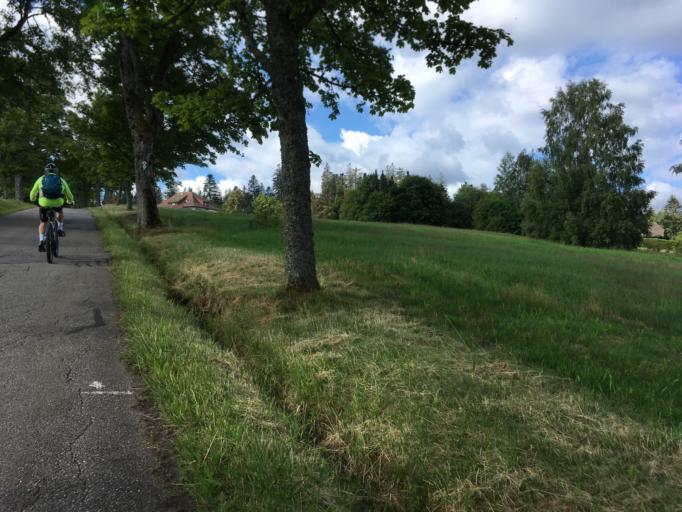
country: DE
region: Baden-Wuerttemberg
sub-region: Karlsruhe Region
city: Freudenstadt
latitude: 48.4551
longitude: 8.4094
